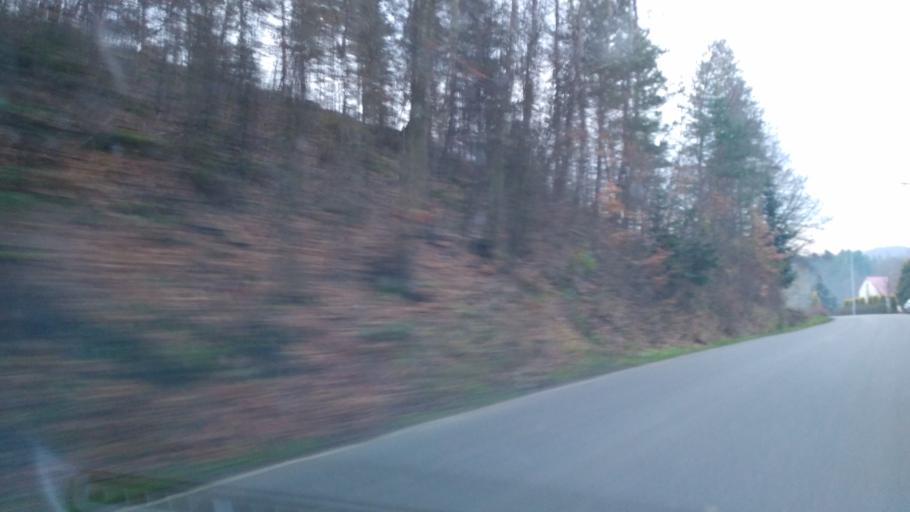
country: PL
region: Subcarpathian Voivodeship
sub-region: Powiat strzyzowski
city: Niebylec
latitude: 49.8606
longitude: 21.8928
